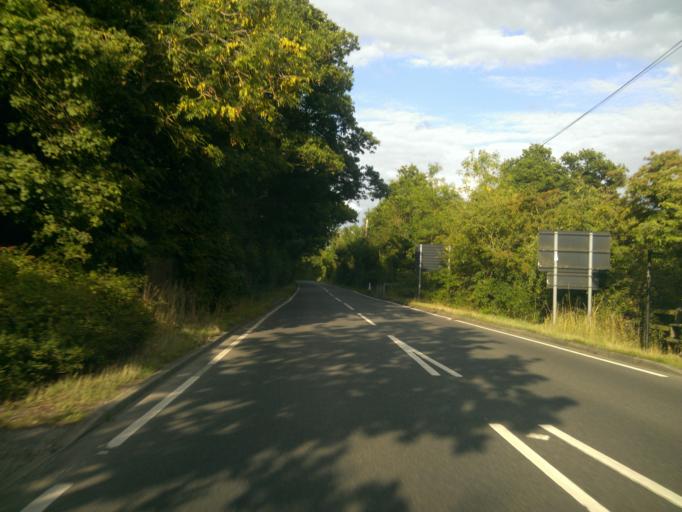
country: GB
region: England
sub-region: Kent
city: Tonbridge
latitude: 51.2101
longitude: 0.2275
